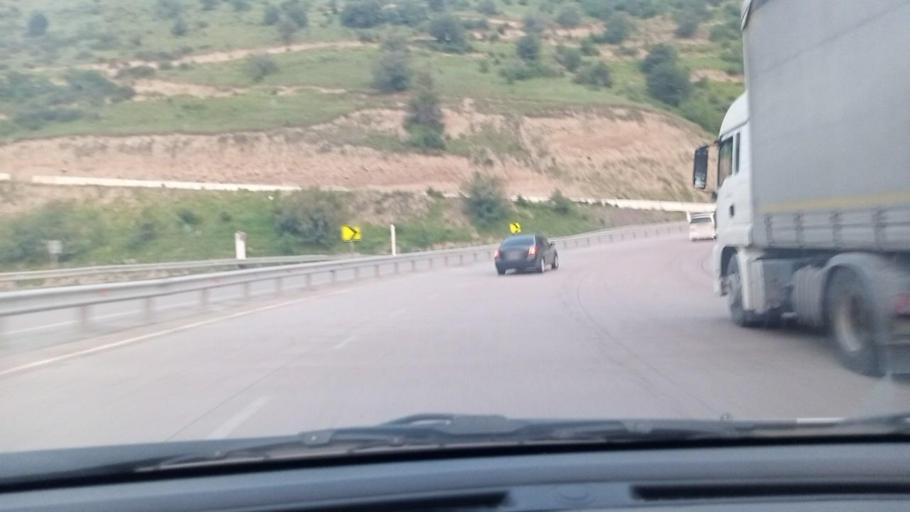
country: UZ
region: Toshkent
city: Angren
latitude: 41.1553
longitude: 70.4477
